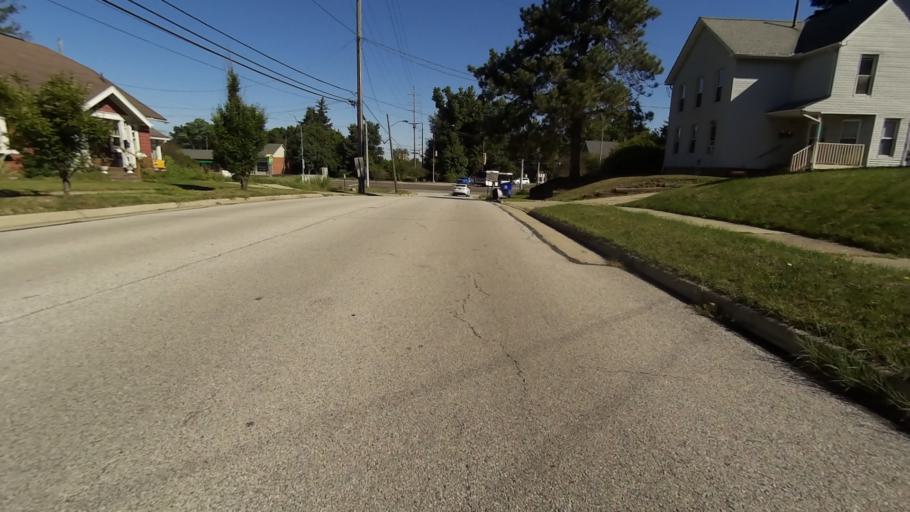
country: US
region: Ohio
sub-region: Portage County
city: Kent
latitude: 41.1504
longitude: -81.3774
